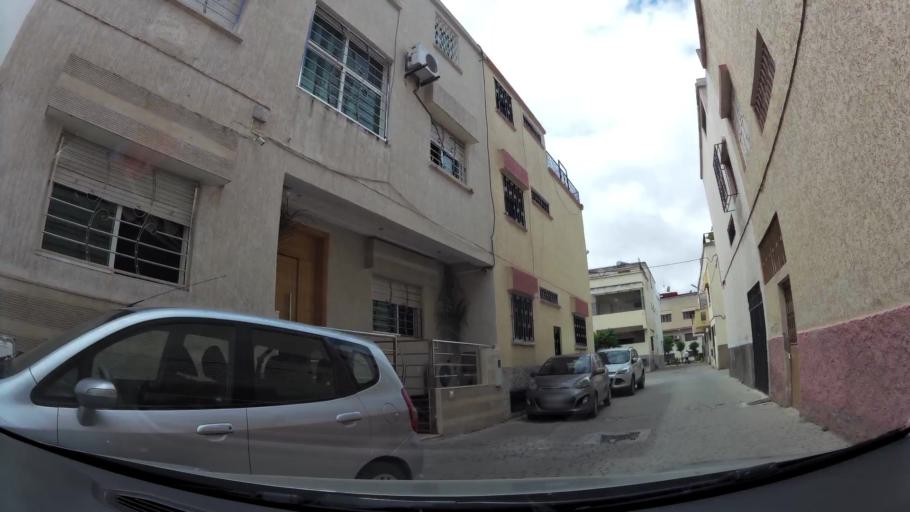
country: MA
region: Fes-Boulemane
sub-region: Fes
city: Fes
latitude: 34.0370
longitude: -5.0168
